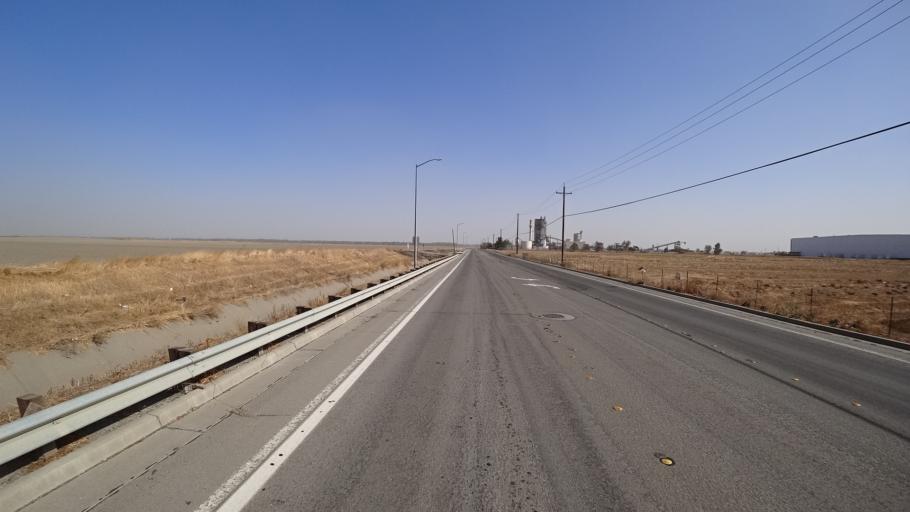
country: US
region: California
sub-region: Yolo County
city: Woodland
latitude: 38.6918
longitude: -121.7431
